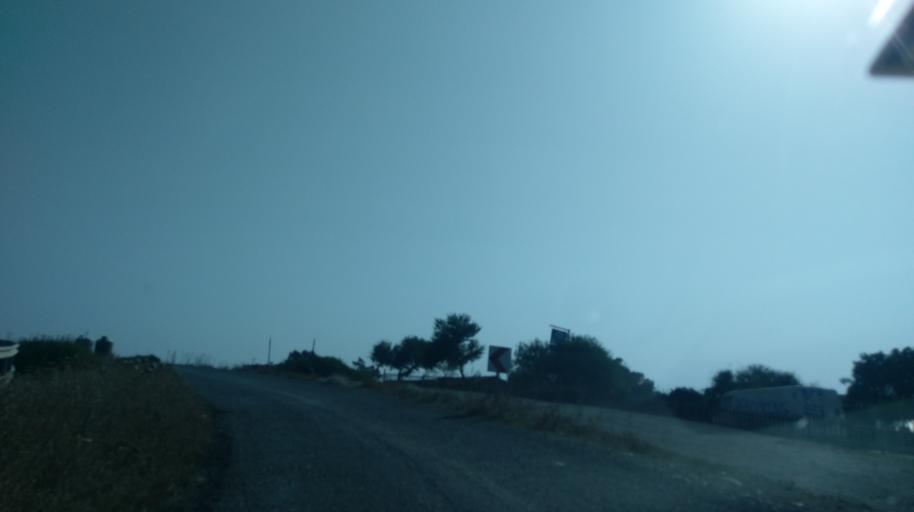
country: CY
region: Ammochostos
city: Rizokarpaso
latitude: 35.6455
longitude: 34.5539
